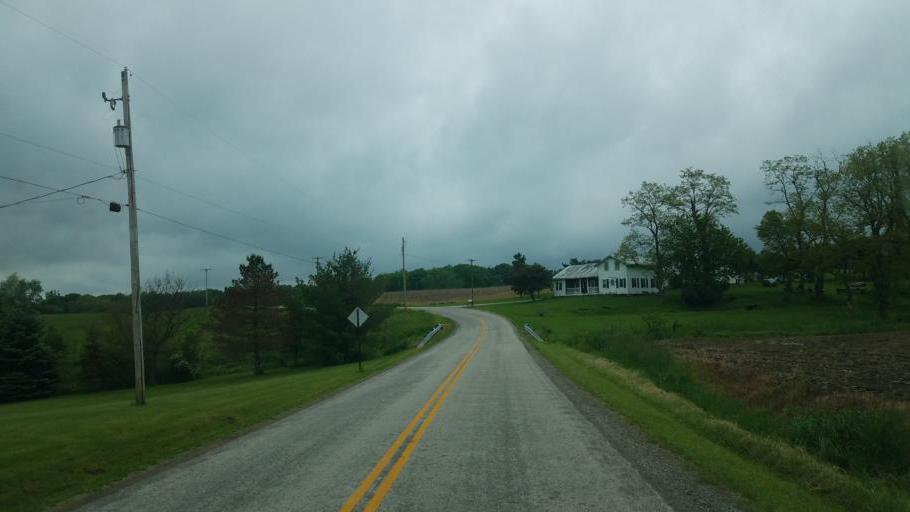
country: US
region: Ohio
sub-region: Ashland County
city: Ashland
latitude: 40.7559
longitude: -82.3235
